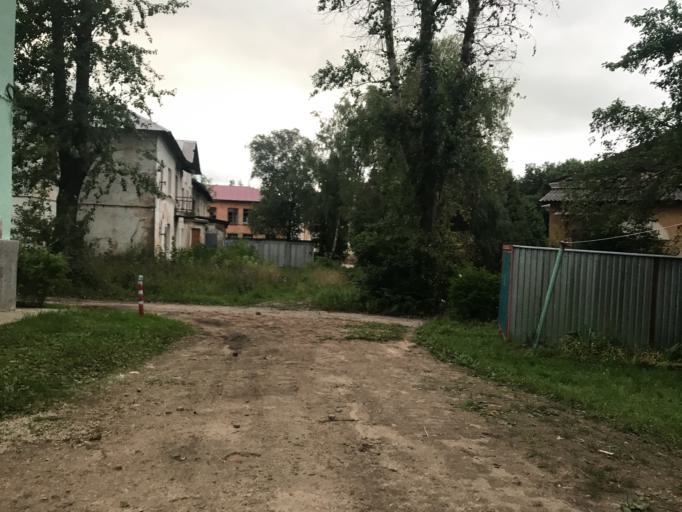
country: RU
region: Tula
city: Priupskiy
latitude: 53.9406
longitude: 37.7021
